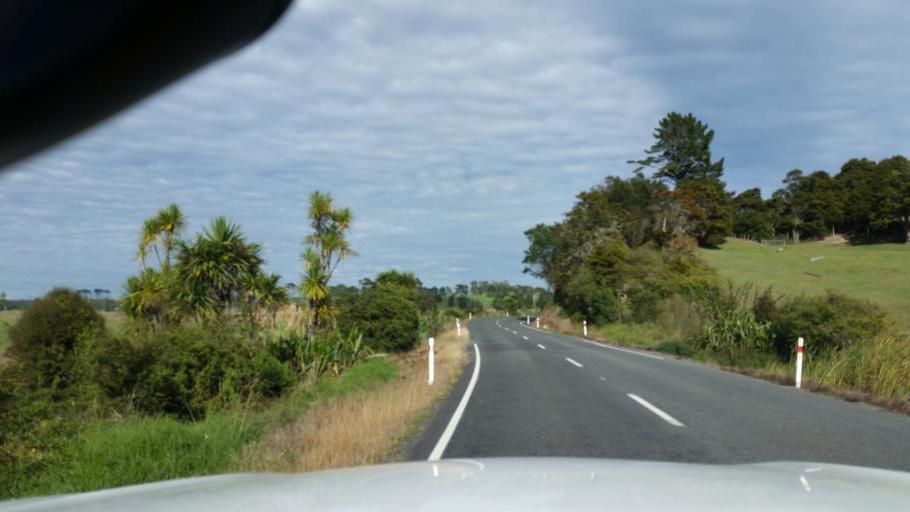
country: NZ
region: Northland
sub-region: Kaipara District
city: Dargaville
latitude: -35.9108
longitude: 173.8400
